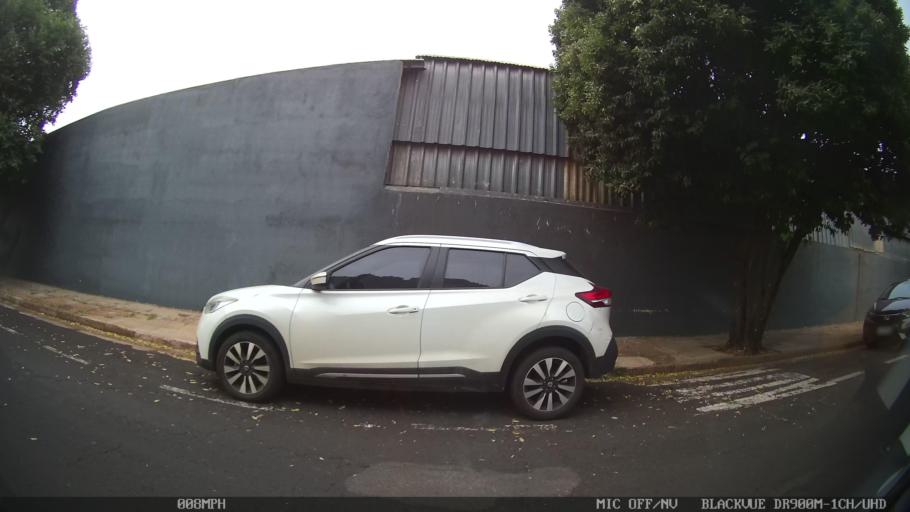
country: BR
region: Sao Paulo
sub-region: Sao Jose Do Rio Preto
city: Sao Jose do Rio Preto
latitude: -20.8287
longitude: -49.3940
